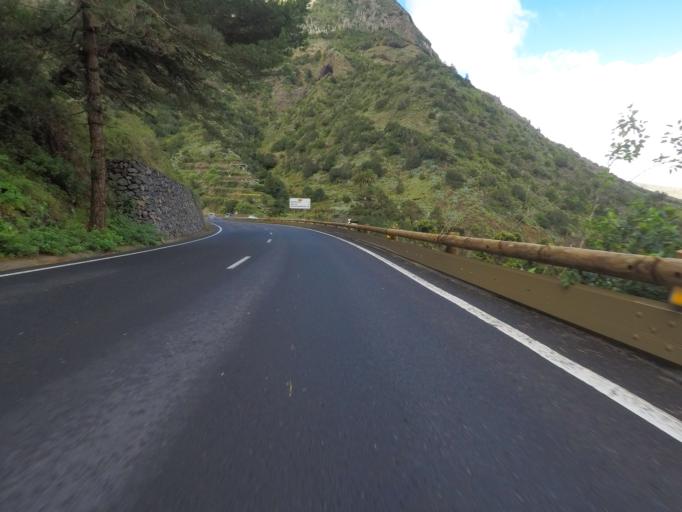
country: ES
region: Canary Islands
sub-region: Provincia de Santa Cruz de Tenerife
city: Hermigua
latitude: 28.1338
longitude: -17.2008
